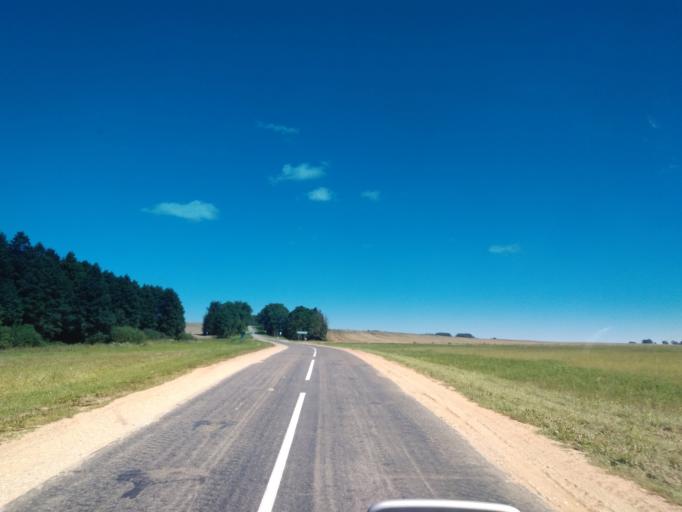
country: BY
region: Minsk
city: Stan'kava
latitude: 53.6382
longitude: 27.2864
